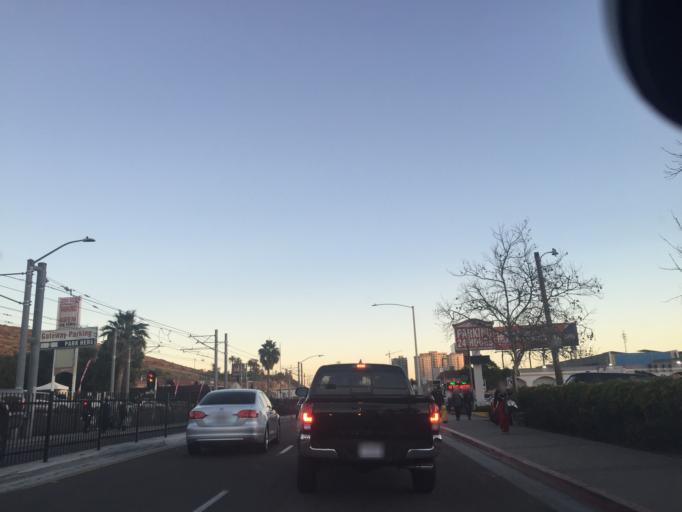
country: MX
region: Baja California
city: Tijuana
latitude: 32.5458
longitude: -117.0311
